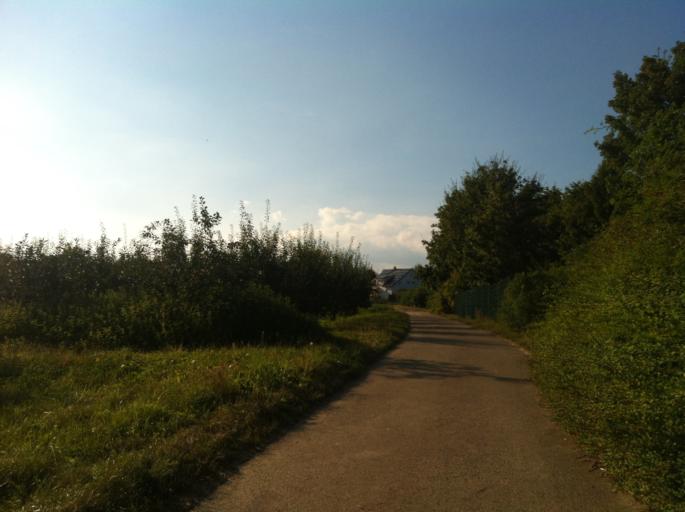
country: DE
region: Rheinland-Pfalz
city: Klein-Winternheim
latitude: 49.9729
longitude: 8.2007
